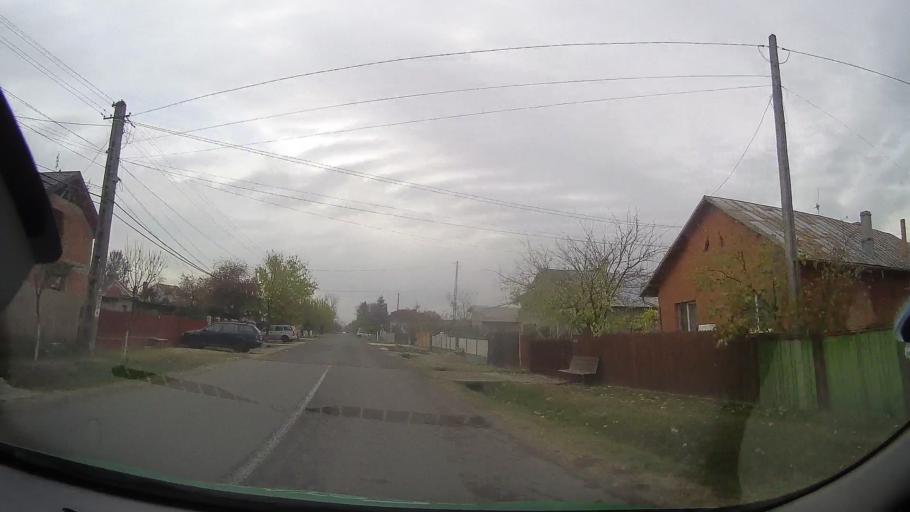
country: RO
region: Prahova
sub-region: Comuna Valea Calugareasca
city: Pantazi
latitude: 44.9215
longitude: 26.1554
